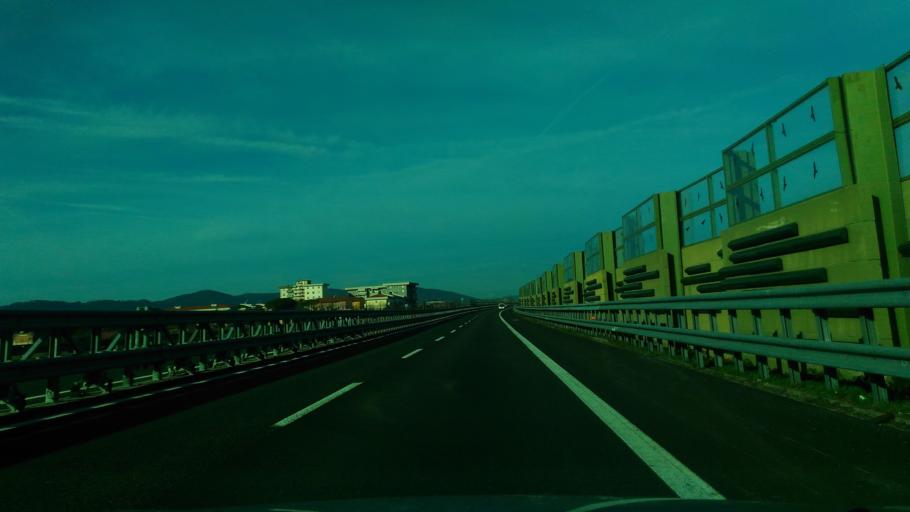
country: IT
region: Tuscany
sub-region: Provincia di Massa-Carrara
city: Carrara
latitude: 44.0422
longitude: 10.0544
